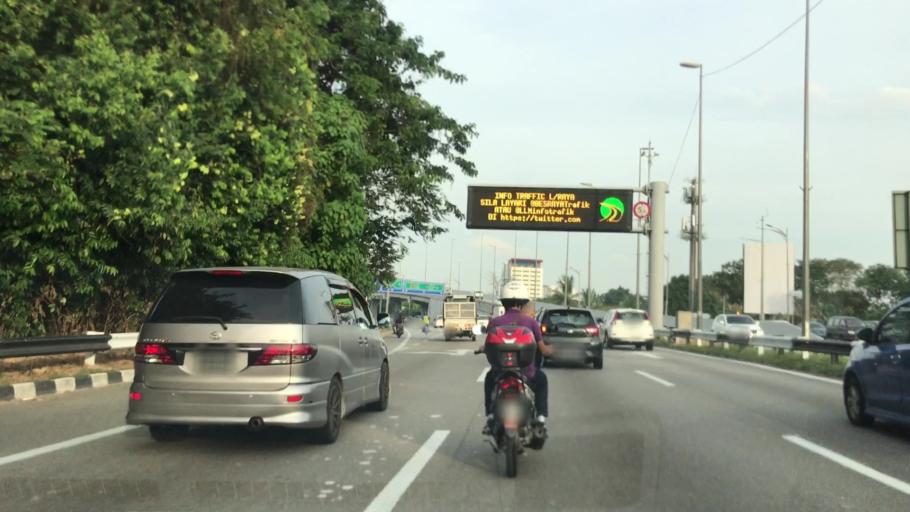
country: MY
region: Kuala Lumpur
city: Kuala Lumpur
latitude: 3.1239
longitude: 101.7037
